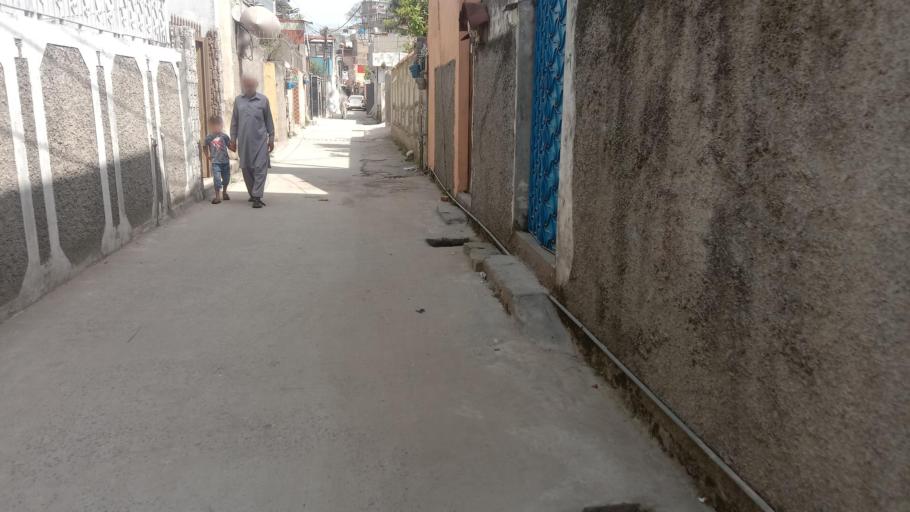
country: PK
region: Khyber Pakhtunkhwa
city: Abbottabad
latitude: 34.1476
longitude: 73.2240
